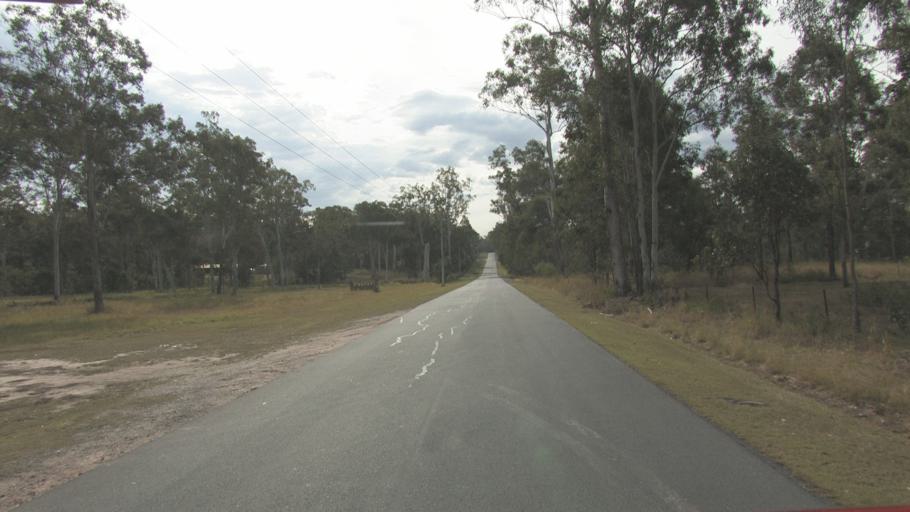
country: AU
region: Queensland
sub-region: Logan
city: Chambers Flat
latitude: -27.7884
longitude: 153.1203
